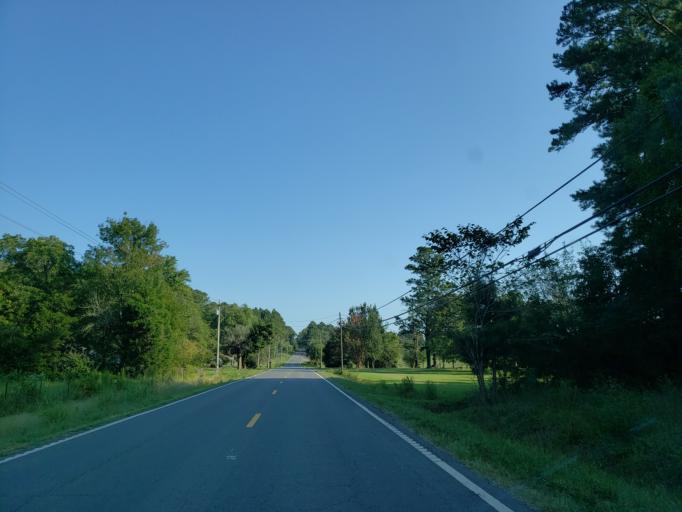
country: US
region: Tennessee
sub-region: Bradley County
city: Wildwood Lake
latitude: 35.0334
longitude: -84.8011
